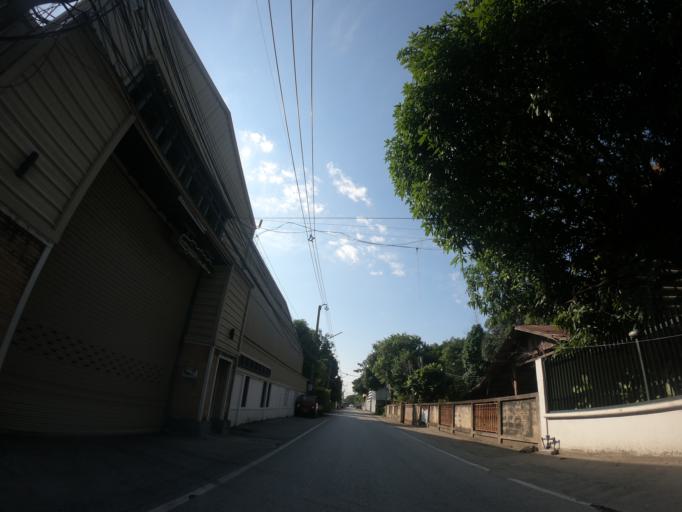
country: TH
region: Chiang Mai
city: Chiang Mai
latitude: 18.7802
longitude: 99.0352
